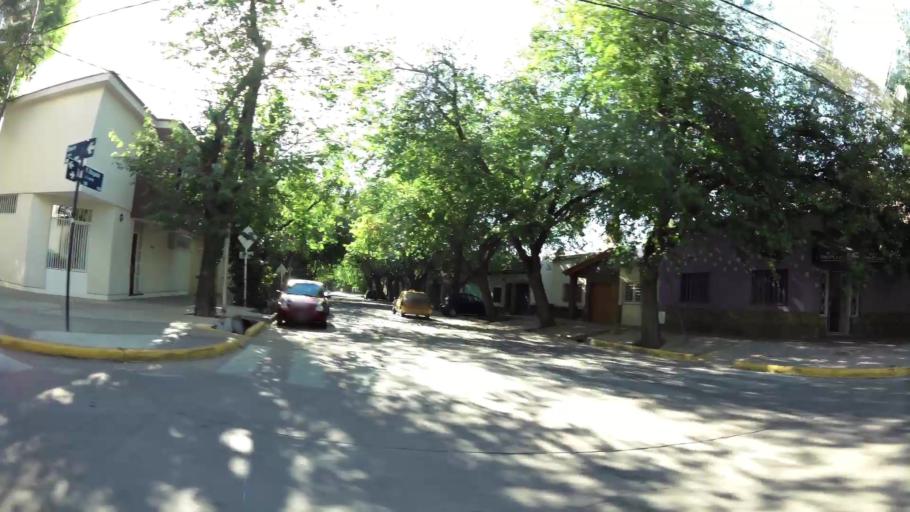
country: AR
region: Mendoza
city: Las Heras
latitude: -32.8698
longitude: -68.8366
